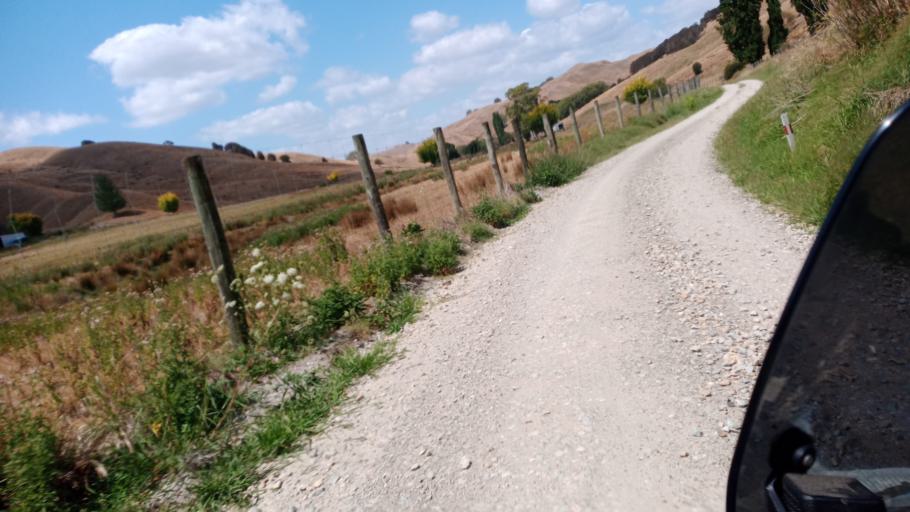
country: NZ
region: Gisborne
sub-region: Gisborne District
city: Gisborne
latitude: -38.4789
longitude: 177.8260
